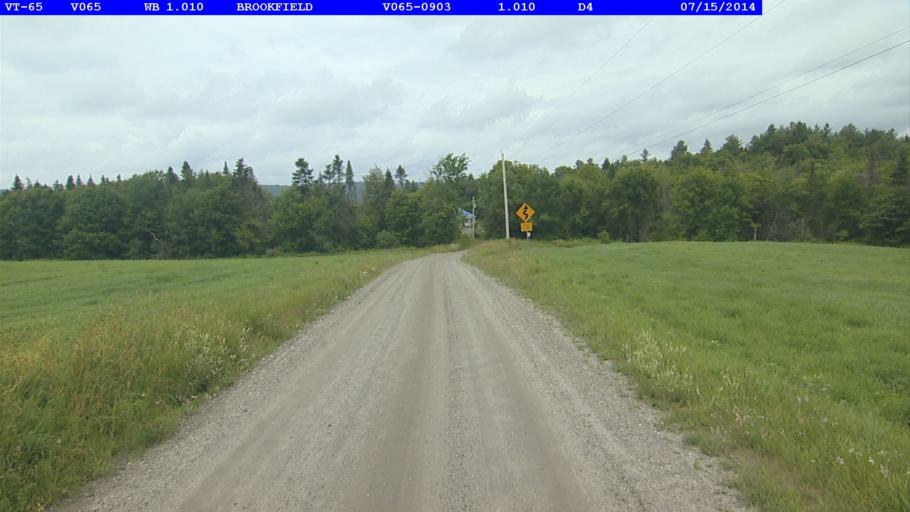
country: US
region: Vermont
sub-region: Washington County
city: Northfield
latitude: 44.0559
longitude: -72.6262
